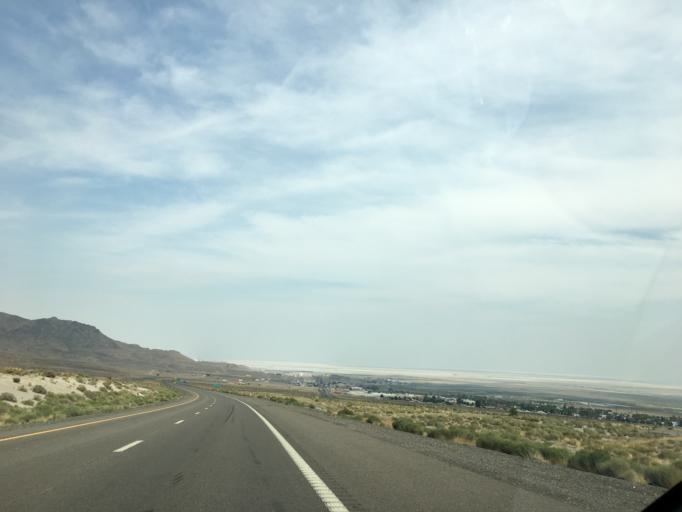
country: US
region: Nevada
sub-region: Elko County
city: West Wendover
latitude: 40.7442
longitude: -114.0957
